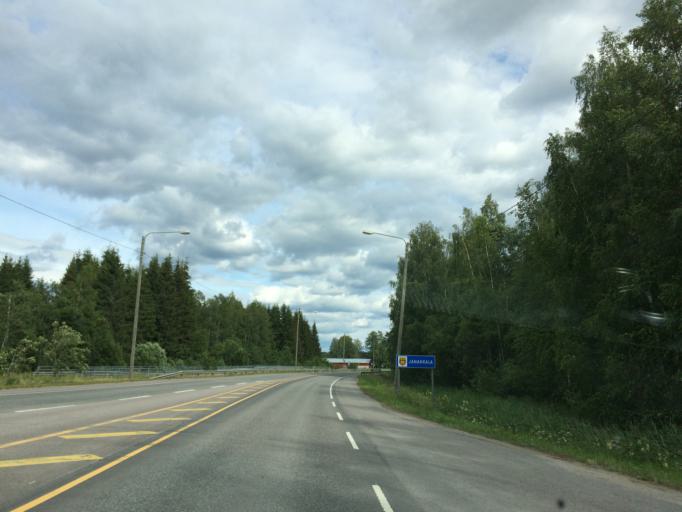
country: FI
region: Haeme
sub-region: Haemeenlinna
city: Janakkala
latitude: 60.9597
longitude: 24.5850
